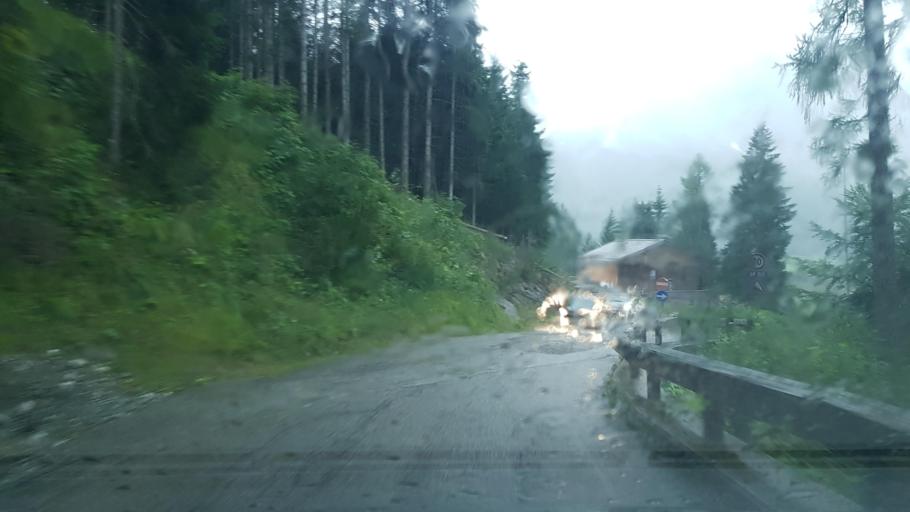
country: IT
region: Veneto
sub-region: Provincia di Belluno
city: Granvilla
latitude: 46.5759
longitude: 12.7247
